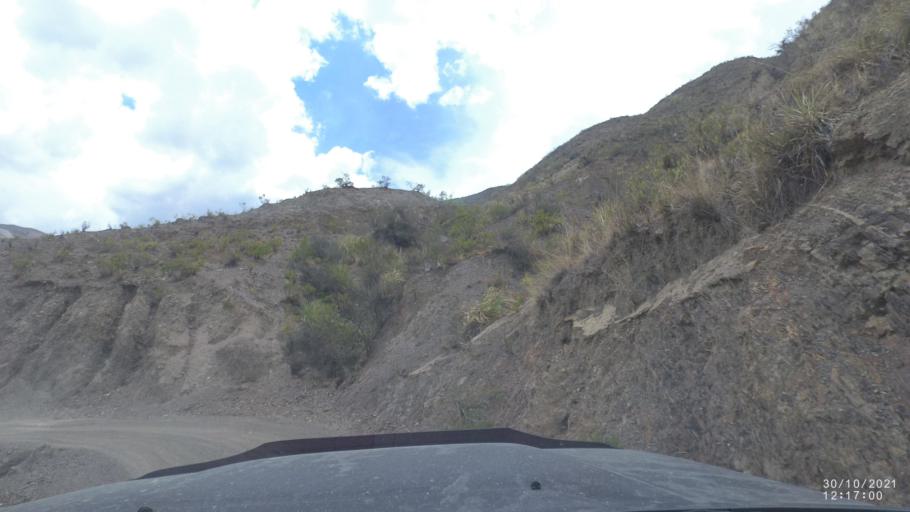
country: BO
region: Cochabamba
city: Colchani
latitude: -17.5644
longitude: -66.6266
